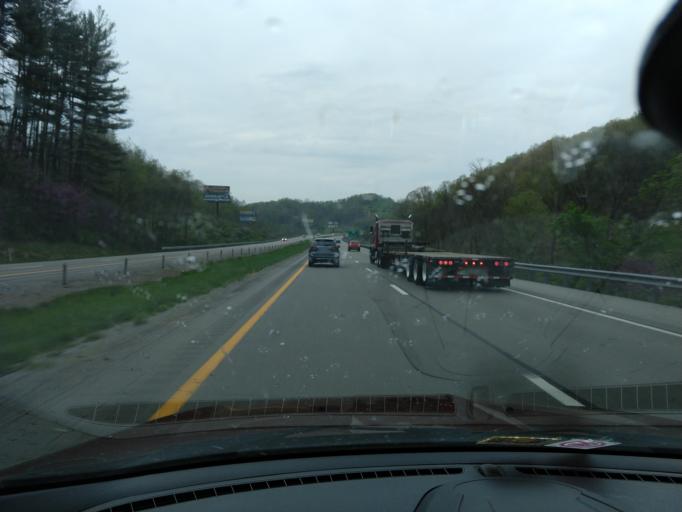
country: US
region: West Virginia
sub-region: Harrison County
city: Stonewood
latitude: 39.1545
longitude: -80.3571
